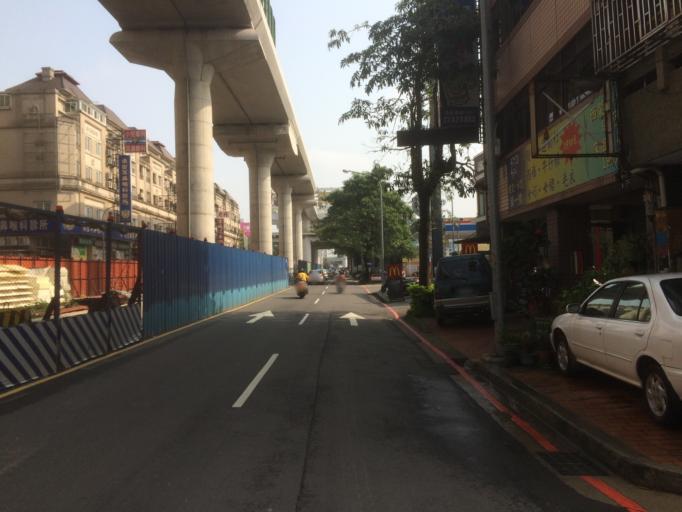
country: TW
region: Taiwan
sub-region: Taichung City
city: Taichung
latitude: 24.1790
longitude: 120.7008
